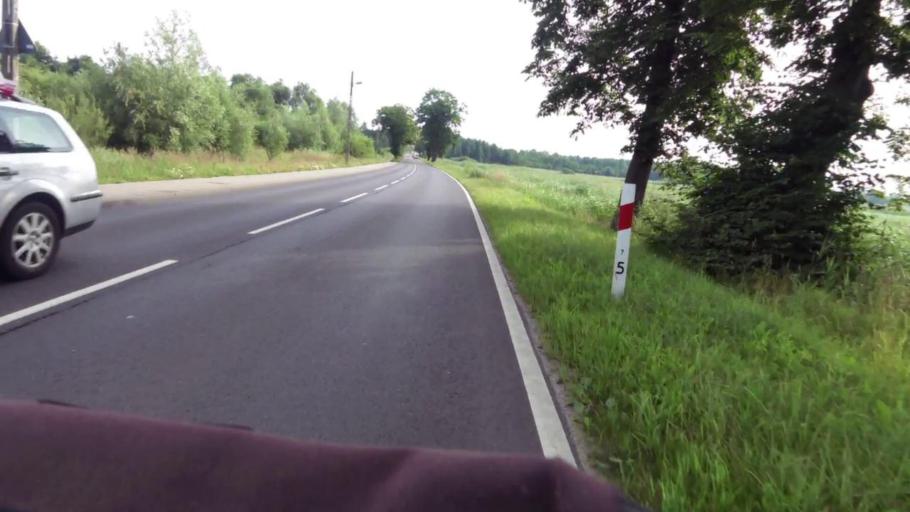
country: PL
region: West Pomeranian Voivodeship
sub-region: Powiat kamienski
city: Kamien Pomorski
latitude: 53.9737
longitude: 14.7877
